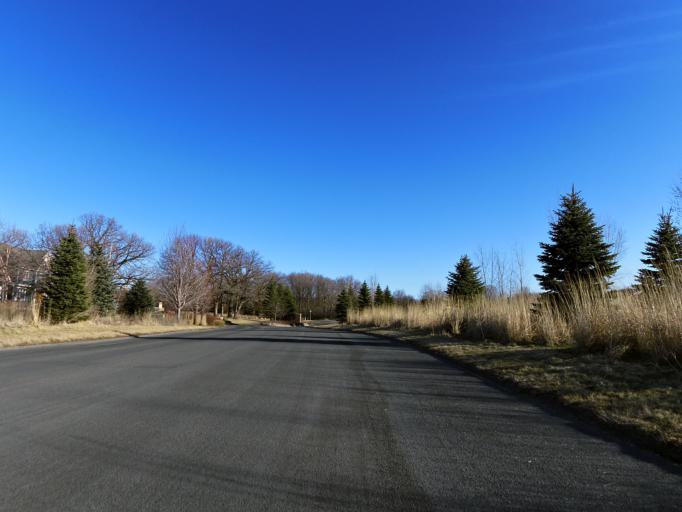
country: US
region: Minnesota
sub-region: Washington County
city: Lakeland
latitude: 44.9770
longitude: -92.7975
